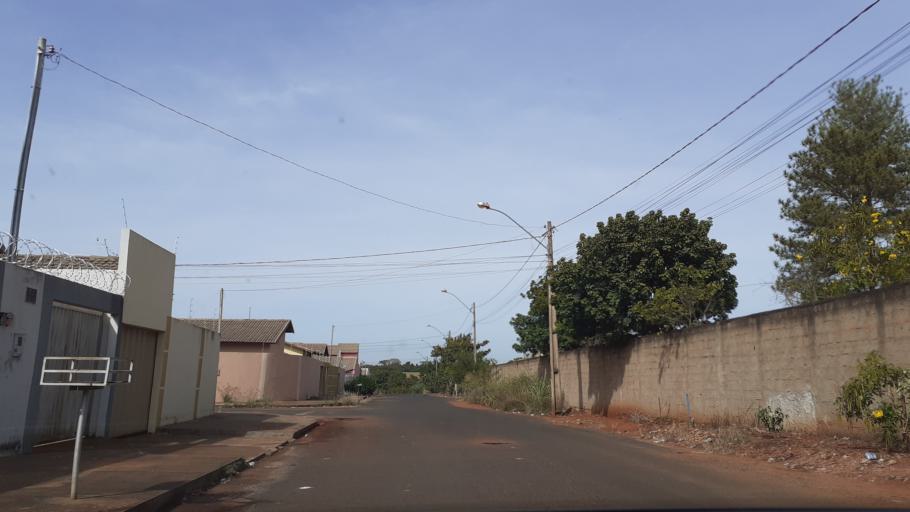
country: BR
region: Goias
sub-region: Itumbiara
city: Itumbiara
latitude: -18.4232
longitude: -49.2458
